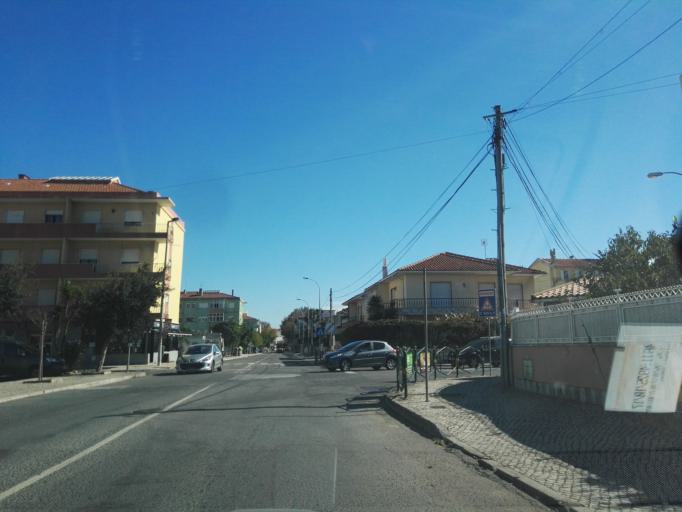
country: PT
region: Lisbon
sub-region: Sintra
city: Sintra
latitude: 38.7979
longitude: -9.3515
